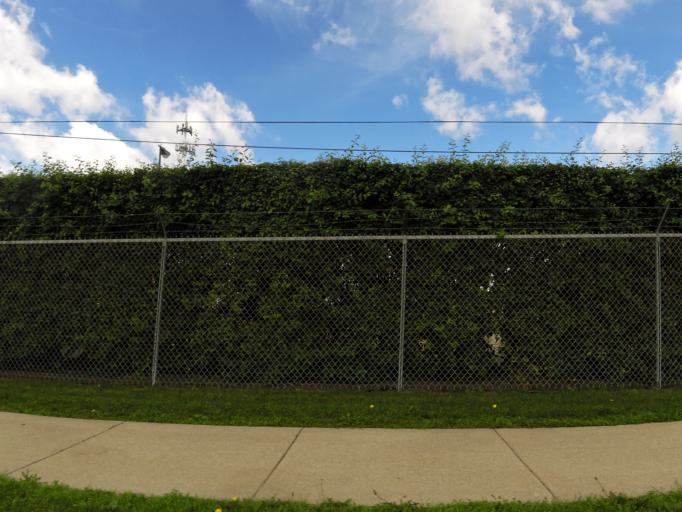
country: US
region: Minnesota
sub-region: Olmsted County
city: Rochester
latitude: 44.0047
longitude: -92.4587
